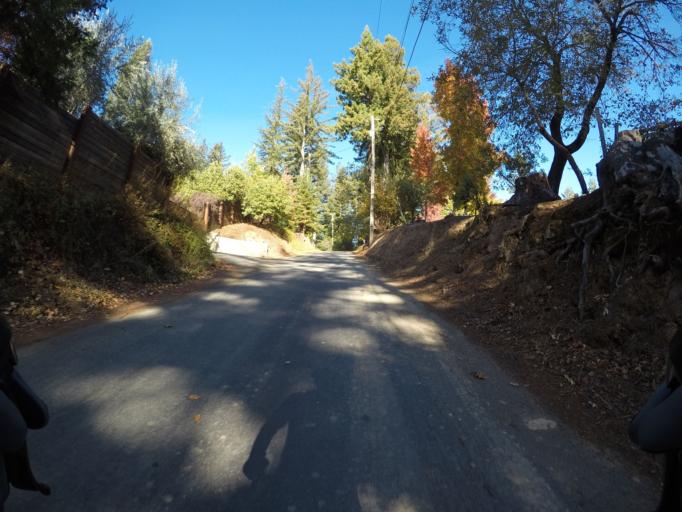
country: US
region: California
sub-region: Santa Clara County
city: Lexington Hills
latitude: 37.1231
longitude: -121.9895
